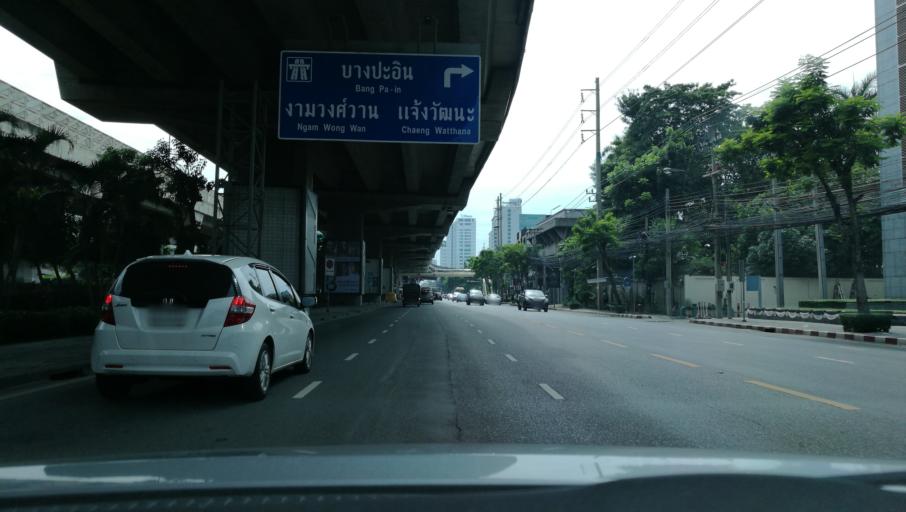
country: TH
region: Bangkok
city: Phaya Thai
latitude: 13.7879
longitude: 100.5361
